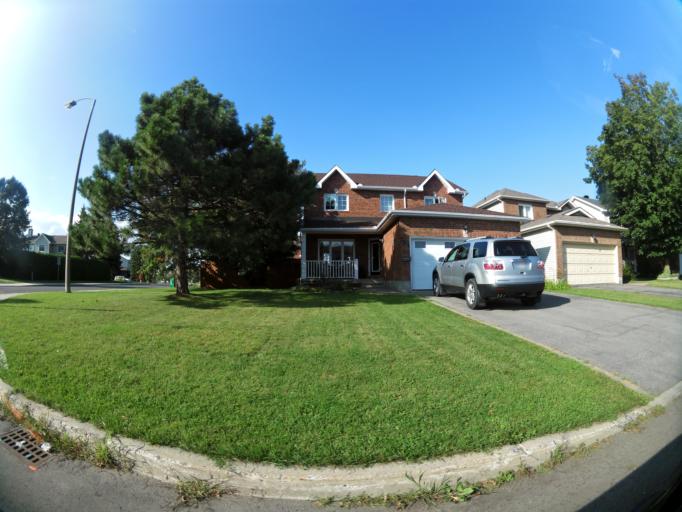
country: CA
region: Ontario
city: Clarence-Rockland
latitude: 45.4825
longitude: -75.4839
